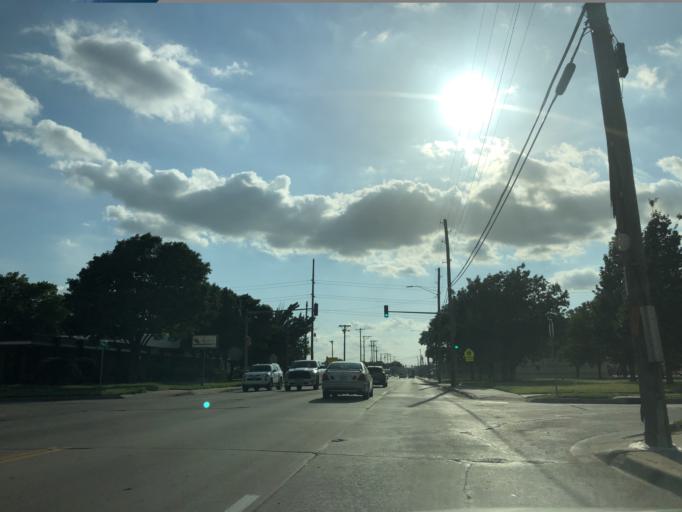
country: US
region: Kansas
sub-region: Sedgwick County
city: Wichita
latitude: 37.7081
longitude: -97.3238
